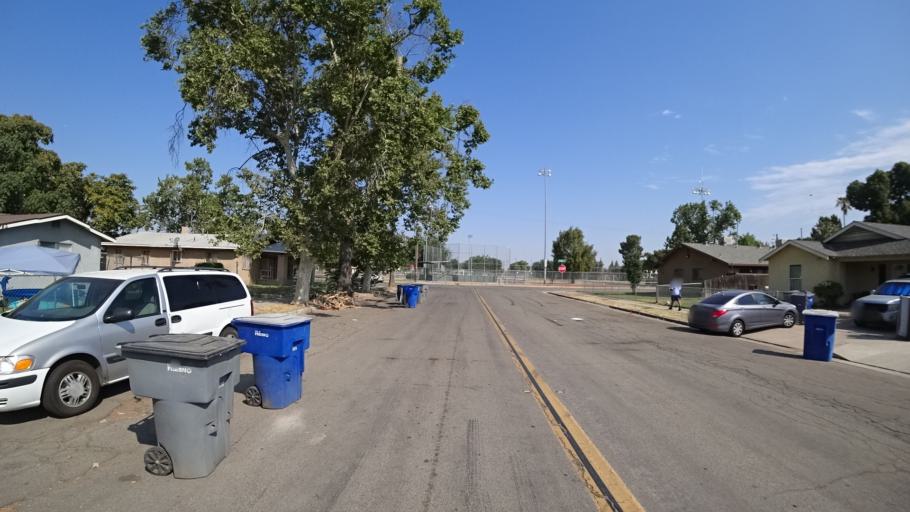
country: US
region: California
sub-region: Fresno County
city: Fresno
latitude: 36.7359
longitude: -119.8064
